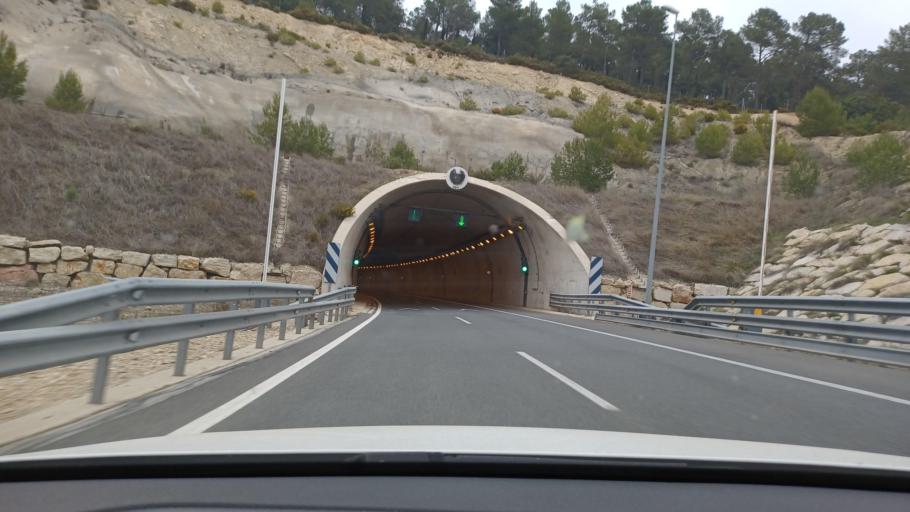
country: ES
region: Valencia
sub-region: Provincia de Alicante
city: Alcoy
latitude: 38.6581
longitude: -0.4648
